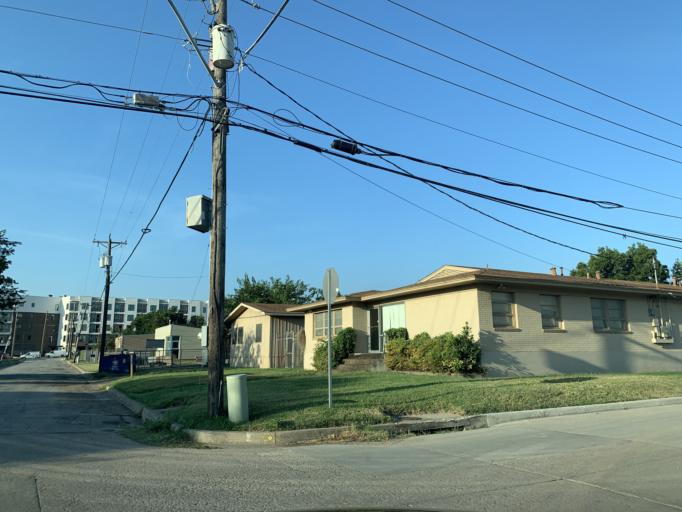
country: US
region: Texas
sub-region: Tarrant County
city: Fort Worth
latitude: 32.7569
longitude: -97.3479
